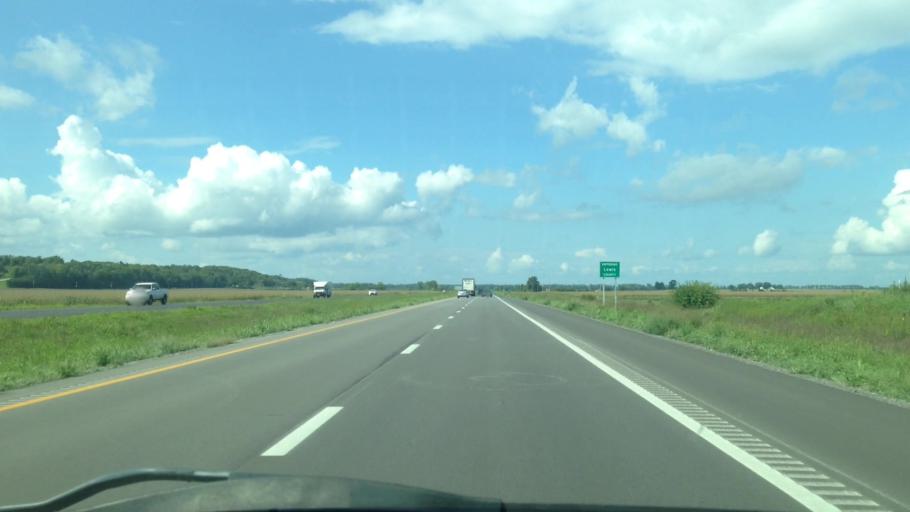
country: US
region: Illinois
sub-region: Adams County
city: Quincy
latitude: 39.9456
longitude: -91.5186
